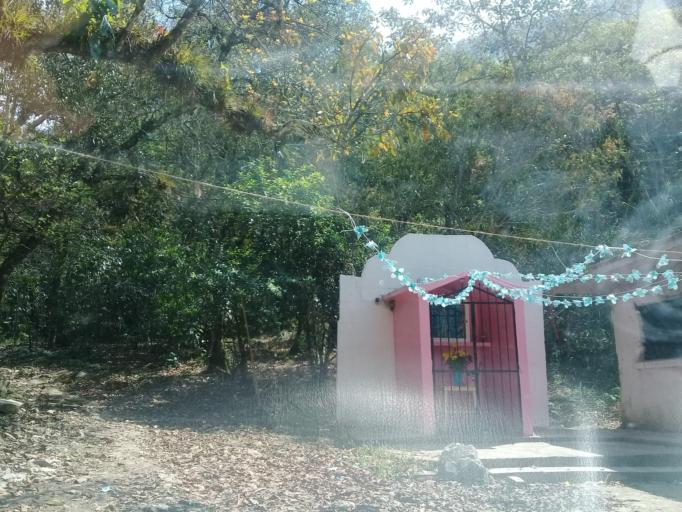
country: MX
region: Veracruz
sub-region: Tlilapan
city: Tonalixco
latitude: 18.8026
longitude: -97.0730
